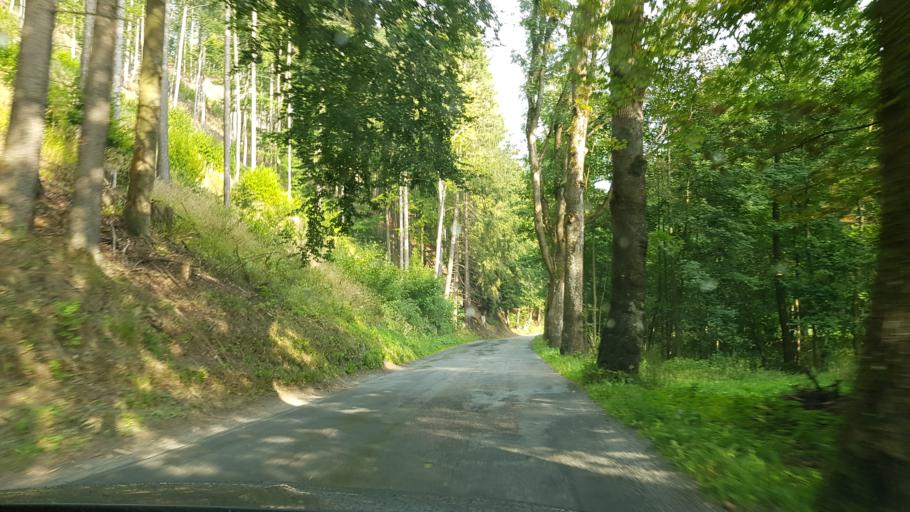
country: CZ
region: Olomoucky
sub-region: Okres Sumperk
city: Hanusovice
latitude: 50.0902
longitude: 16.8854
